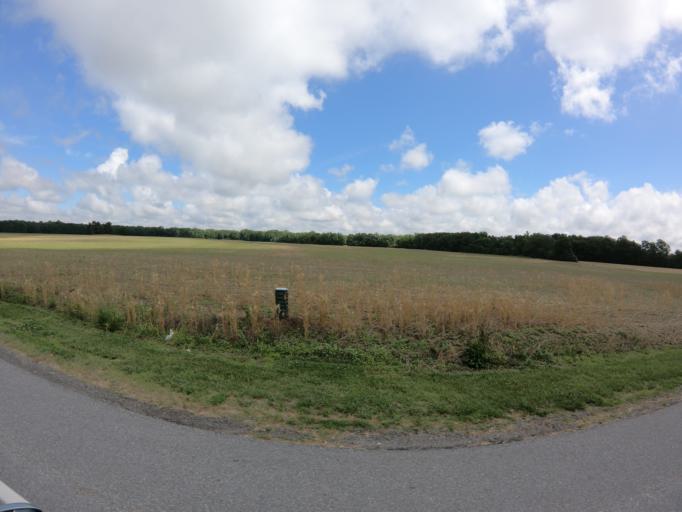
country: US
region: Maryland
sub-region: Queen Anne's County
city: Kingstown
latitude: 39.1209
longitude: -75.9336
